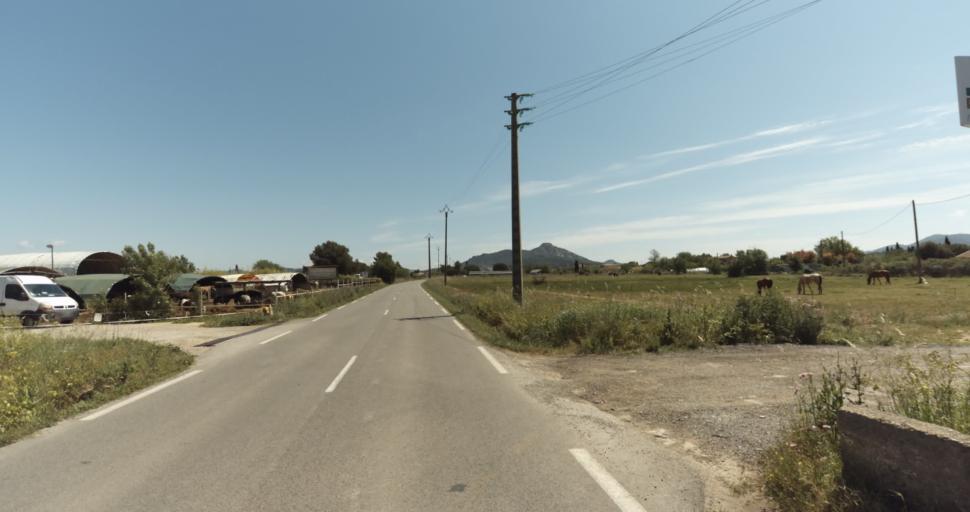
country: FR
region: Provence-Alpes-Cote d'Azur
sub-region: Departement du Var
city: La Crau
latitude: 43.1407
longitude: 6.0519
